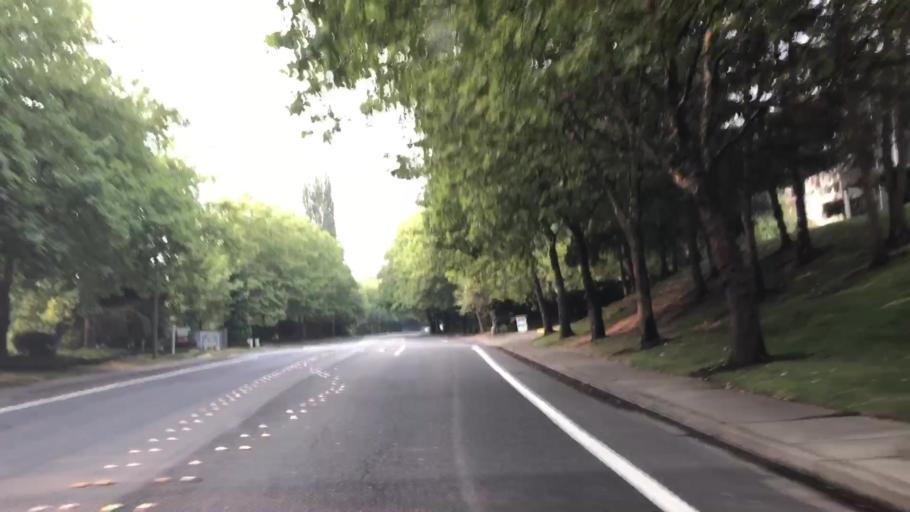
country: US
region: Washington
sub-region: King County
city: Redmond
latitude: 47.6701
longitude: -122.1333
